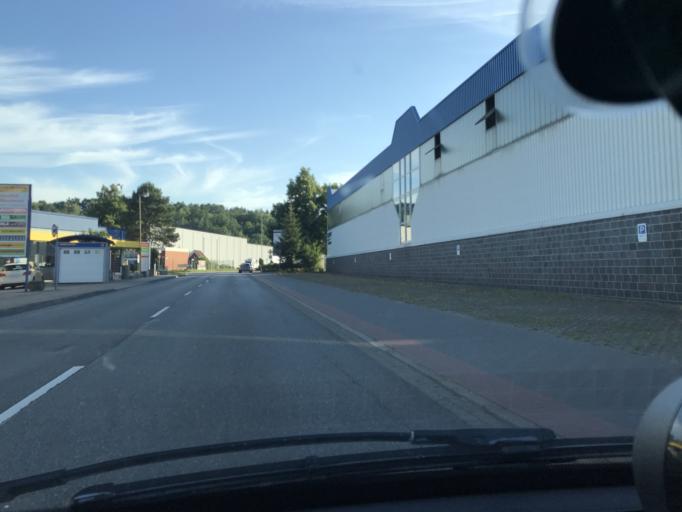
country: DE
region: Lower Saxony
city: Buxtehude
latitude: 53.4632
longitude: 9.7173
